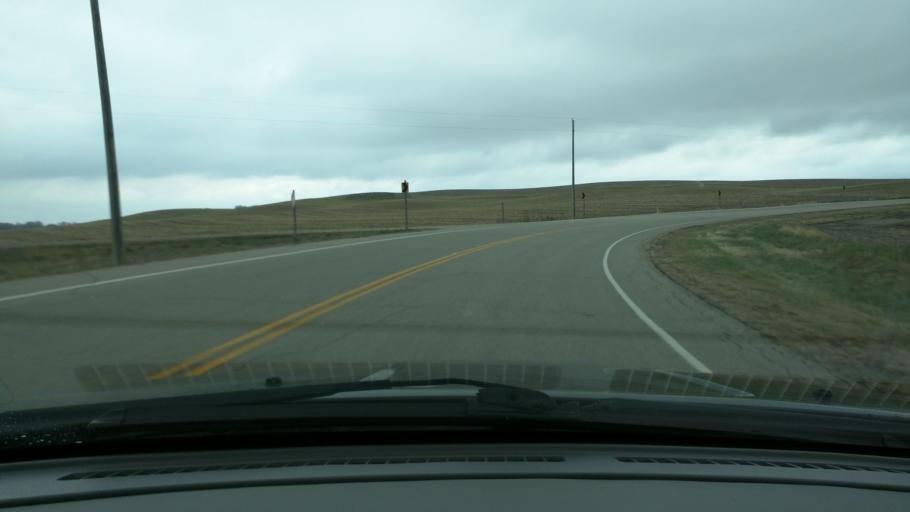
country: US
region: Minnesota
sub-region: Washington County
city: Cottage Grove
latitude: 44.7638
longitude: -92.9246
